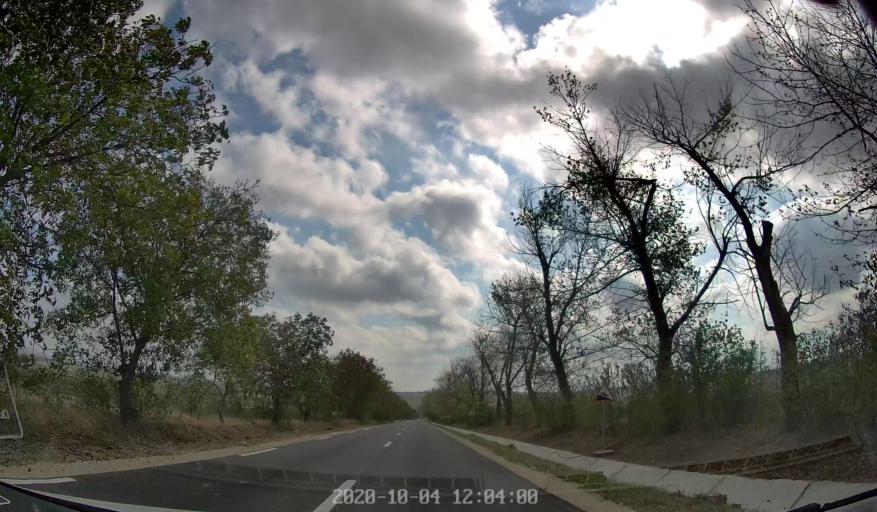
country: MD
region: Rezina
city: Saharna
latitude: 47.6075
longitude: 28.9366
